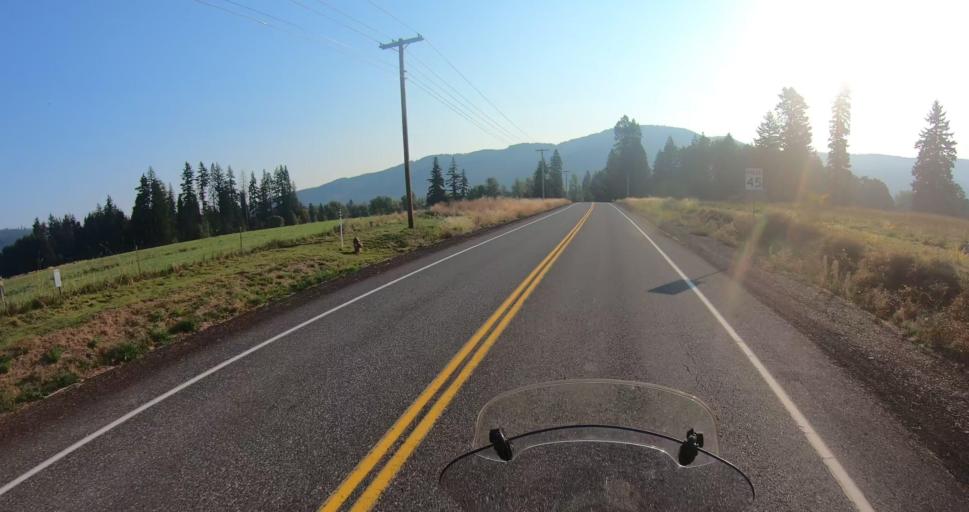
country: US
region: Oregon
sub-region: Hood River County
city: Odell
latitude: 45.5417
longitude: -121.5880
